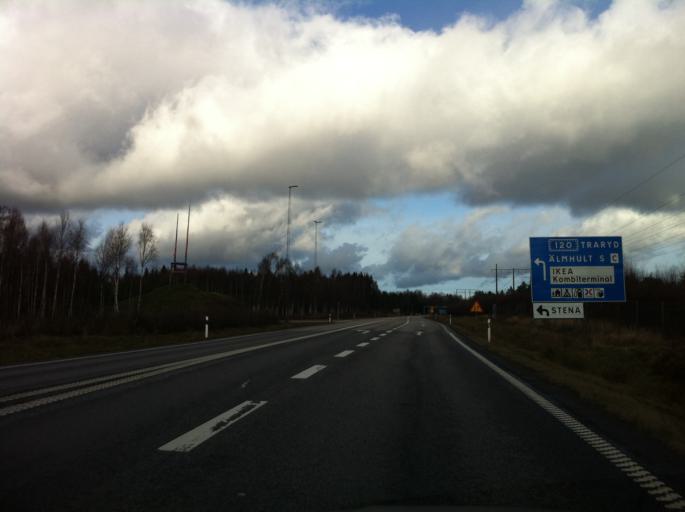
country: SE
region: Kronoberg
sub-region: Almhults Kommun
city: AElmhult
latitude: 56.5139
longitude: 14.1333
